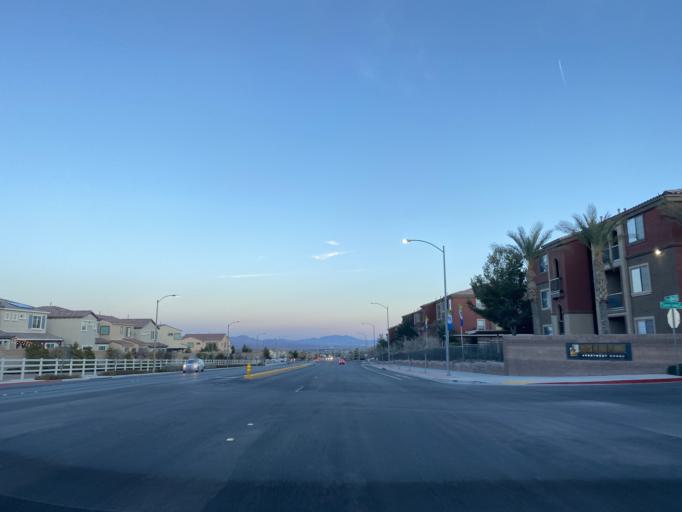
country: US
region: Nevada
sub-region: Clark County
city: Summerlin South
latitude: 36.3066
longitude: -115.3087
